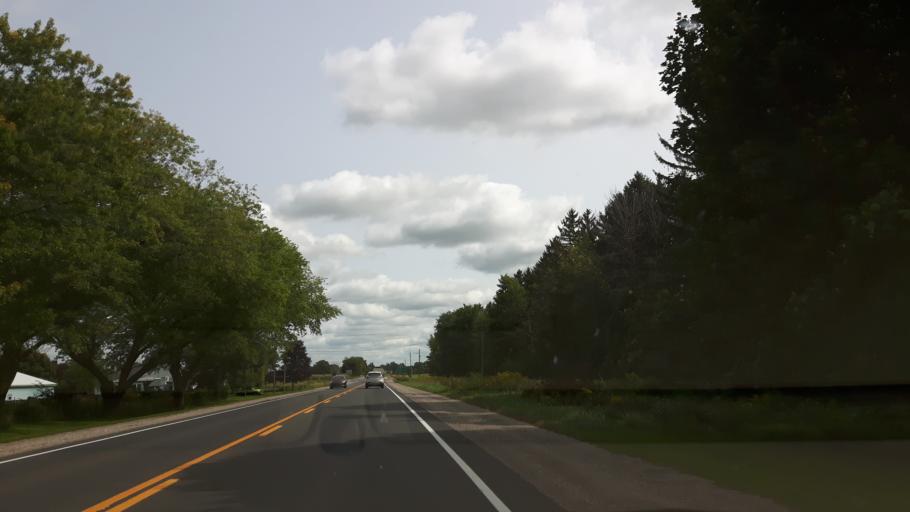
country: CA
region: Ontario
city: Huron East
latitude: 43.5831
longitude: -81.4613
